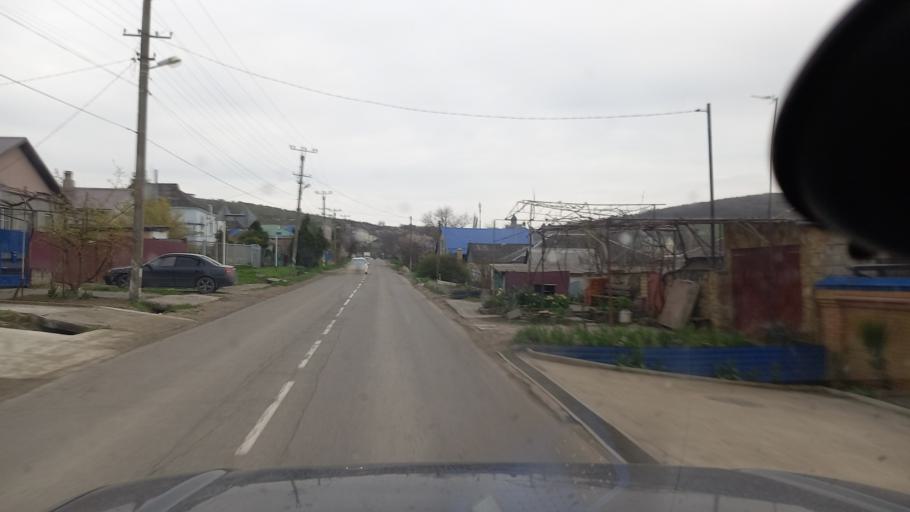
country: RU
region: Krasnodarskiy
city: Sukko
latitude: 44.8499
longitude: 37.4361
